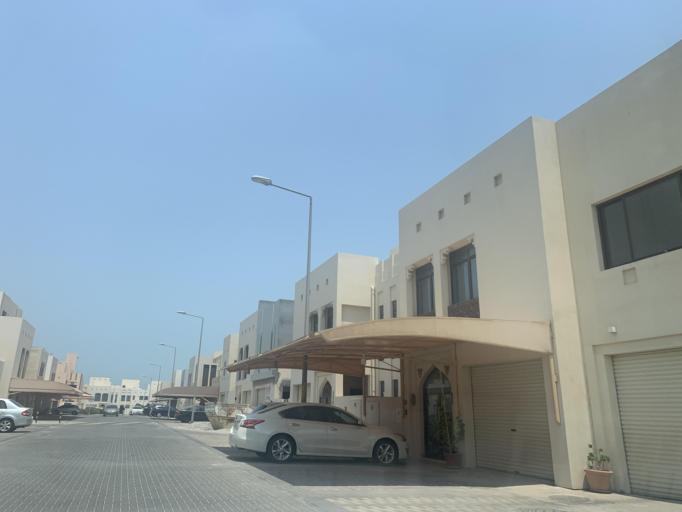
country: BH
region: Muharraq
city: Al Hadd
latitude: 26.2348
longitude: 50.6695
